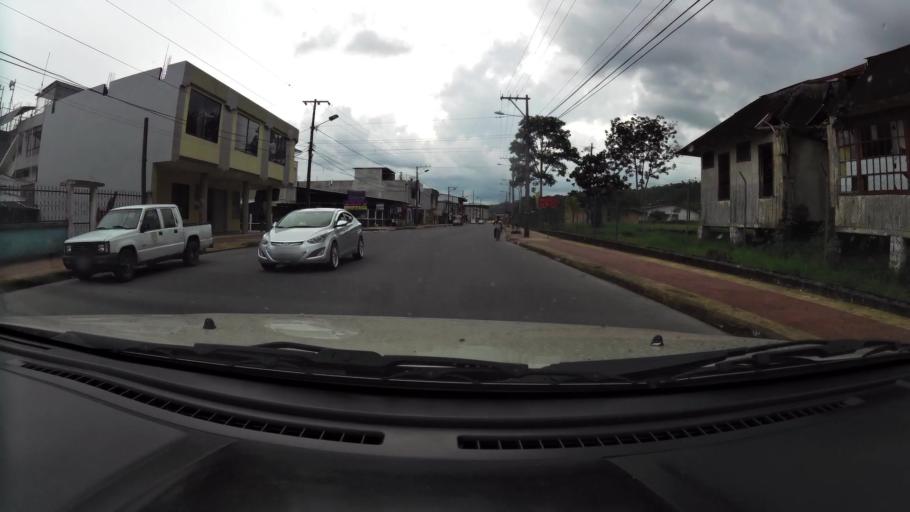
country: EC
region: Pastaza
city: Puyo
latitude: -1.4905
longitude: -78.0129
